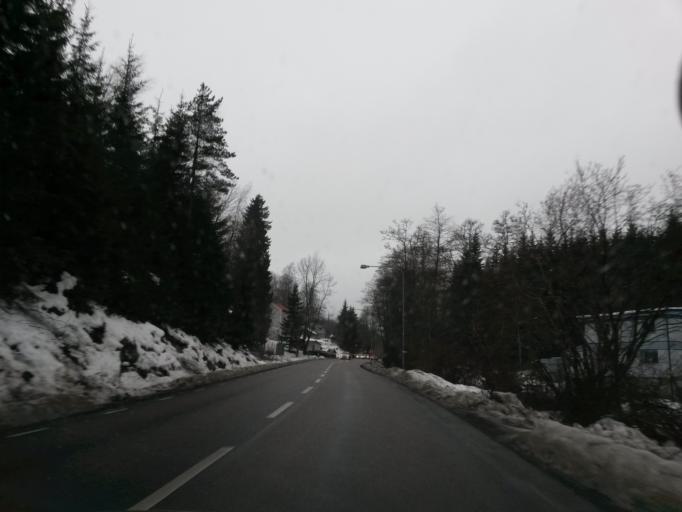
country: SE
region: Vaestra Goetaland
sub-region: Boras Kommun
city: Boras
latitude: 57.7445
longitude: 12.8928
